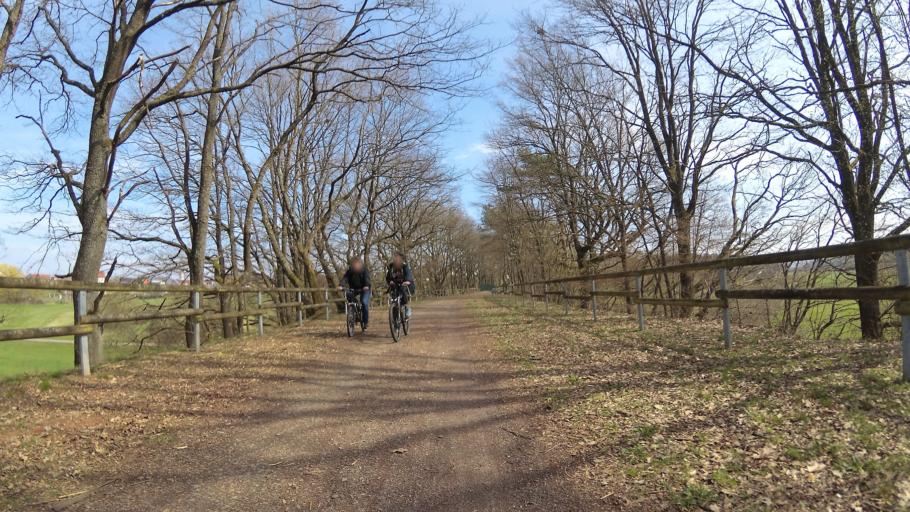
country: DE
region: Rheinland-Pfalz
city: Gries
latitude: 49.4090
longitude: 7.3910
